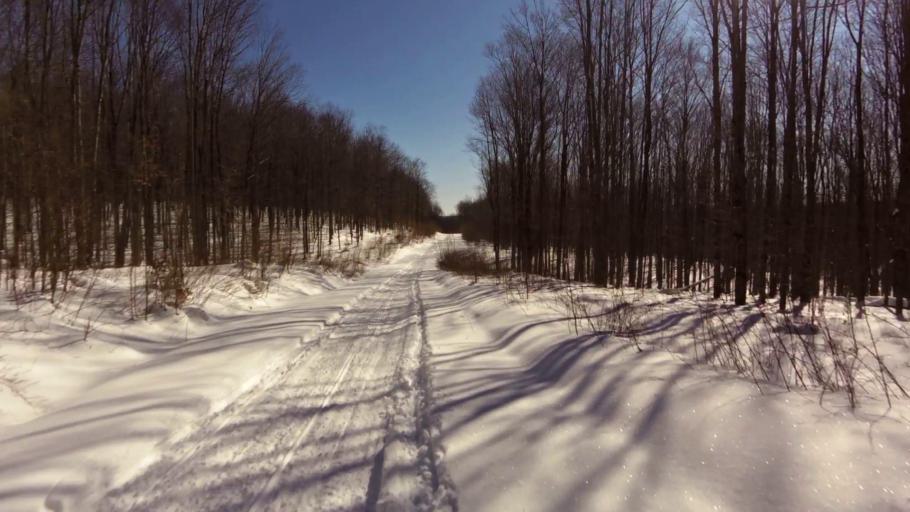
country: US
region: New York
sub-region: Cattaraugus County
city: Franklinville
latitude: 42.3489
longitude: -78.3367
